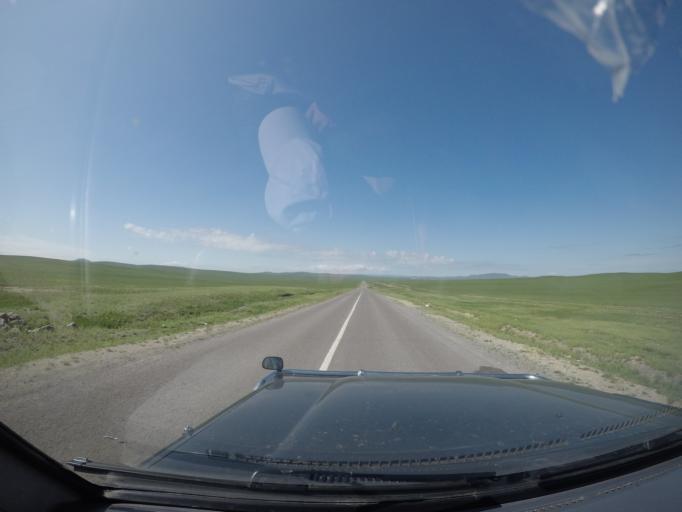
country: MN
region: Suhbaatar
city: Bayasgalant
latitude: 47.3491
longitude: 111.6359
